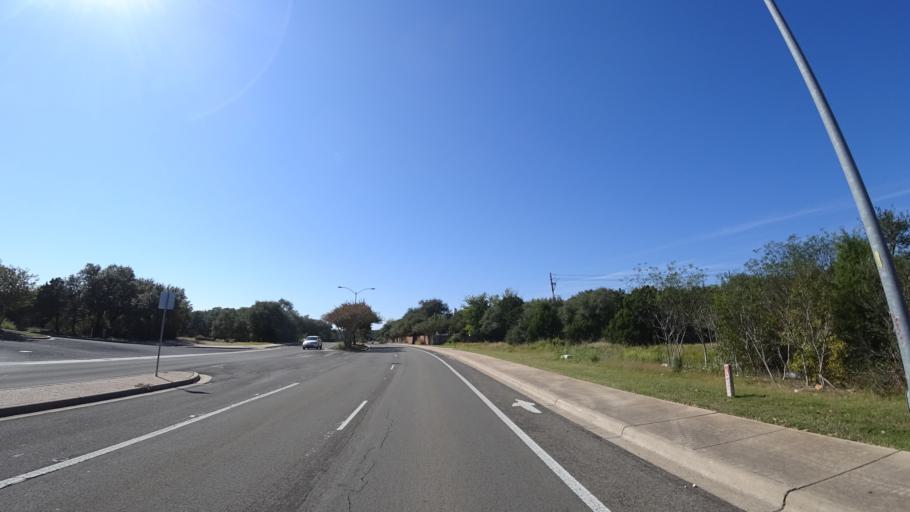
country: US
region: Texas
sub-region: Travis County
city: Shady Hollow
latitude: 30.2088
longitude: -97.8639
